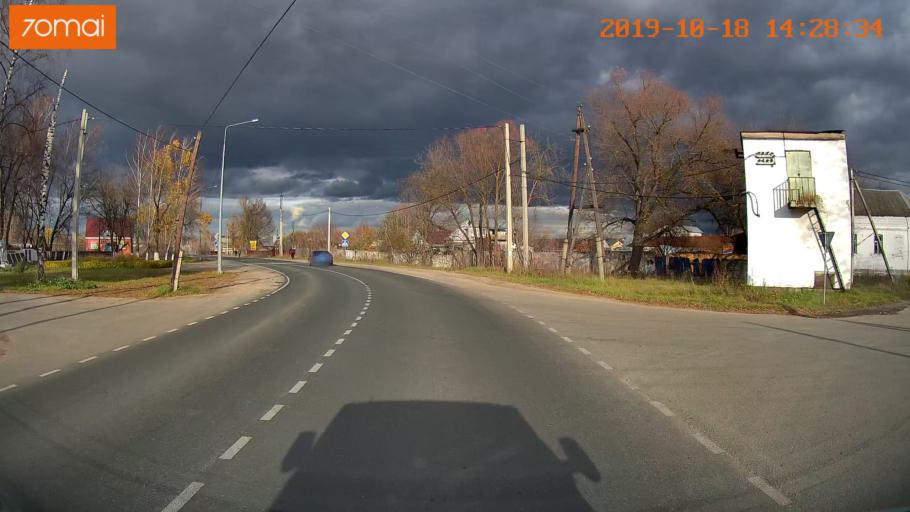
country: RU
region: Rjazan
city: Tuma
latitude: 55.1493
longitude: 40.5541
